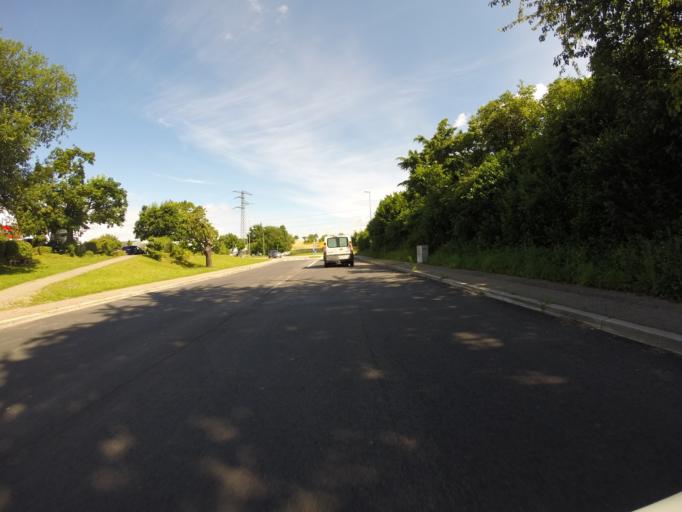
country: DE
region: Baden-Wuerttemberg
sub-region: Karlsruhe Region
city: Ettlingen
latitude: 48.9200
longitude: 8.5056
